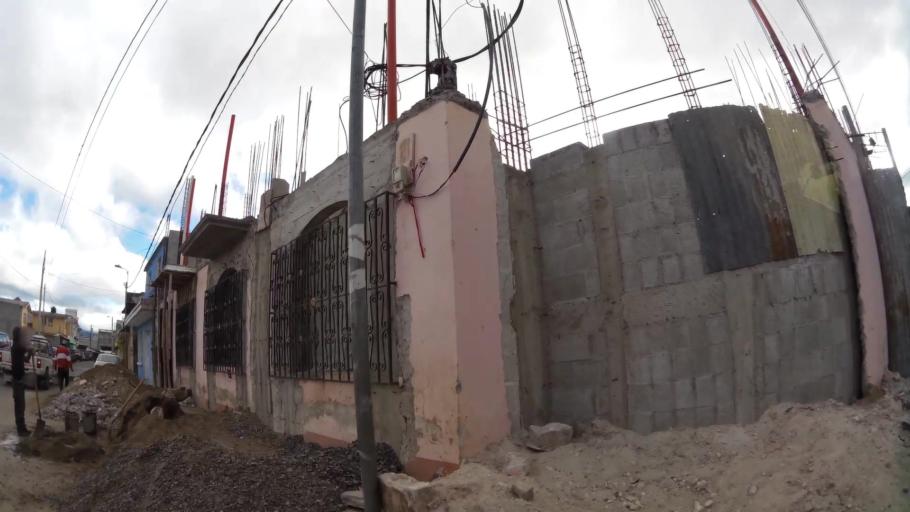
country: GT
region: Quetzaltenango
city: Salcaja
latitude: 14.8768
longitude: -91.4587
